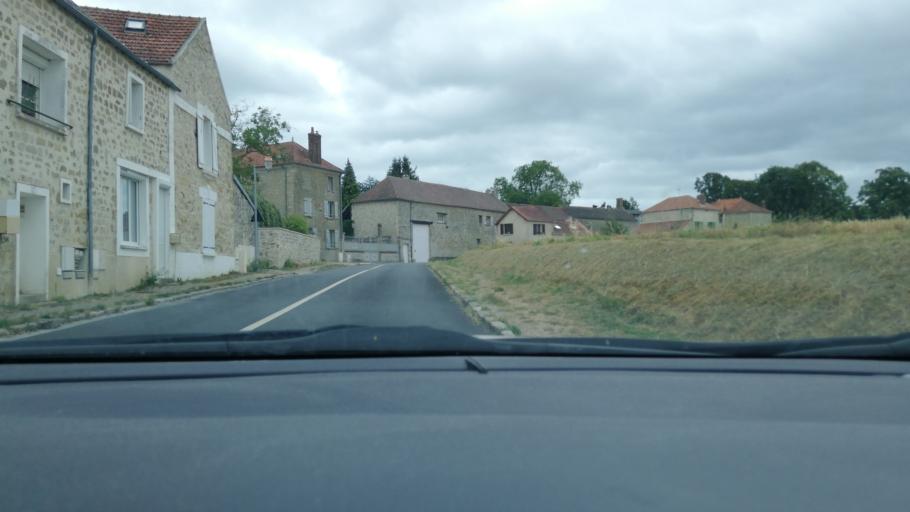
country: FR
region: Ile-de-France
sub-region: Departement du Val-d'Oise
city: Ennery
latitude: 49.1036
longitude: 2.1328
